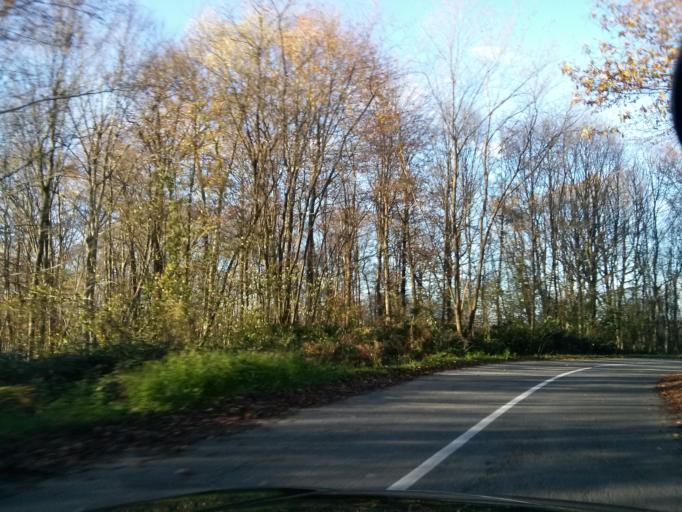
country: HR
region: Sisacko-Moslavacka
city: Gvozd
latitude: 45.3714
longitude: 15.9095
